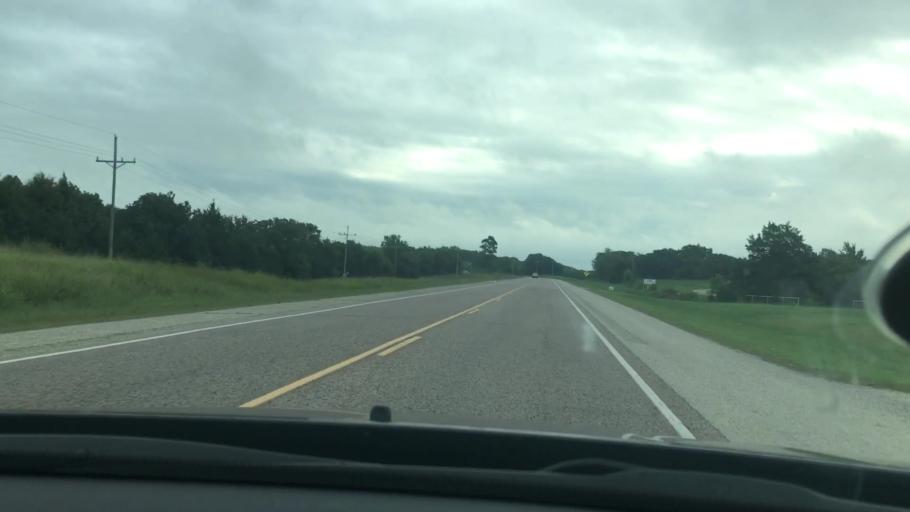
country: US
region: Oklahoma
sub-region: Pontotoc County
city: Ada
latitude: 34.7976
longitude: -96.5489
